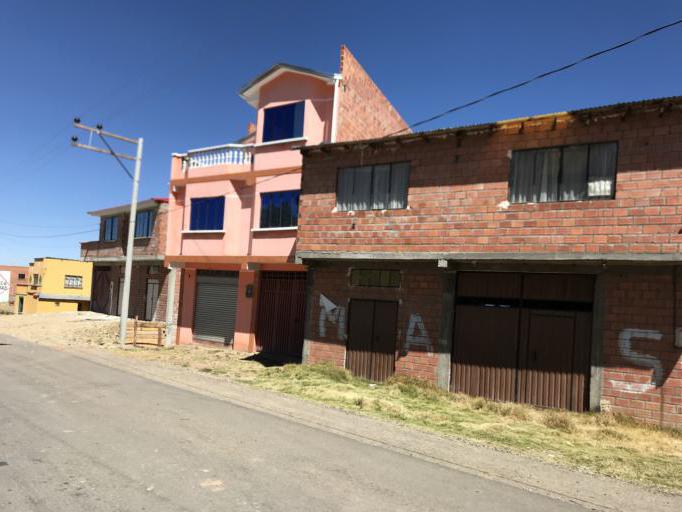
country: BO
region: La Paz
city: Huatajata
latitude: -16.2036
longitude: -68.7083
